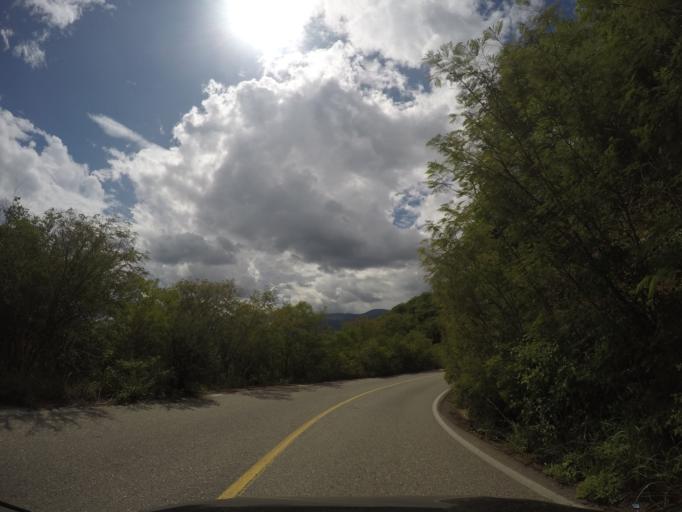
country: MX
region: Oaxaca
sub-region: San Jeronimo Coatlan
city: San Cristobal Honduras
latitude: 16.4337
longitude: -97.0500
